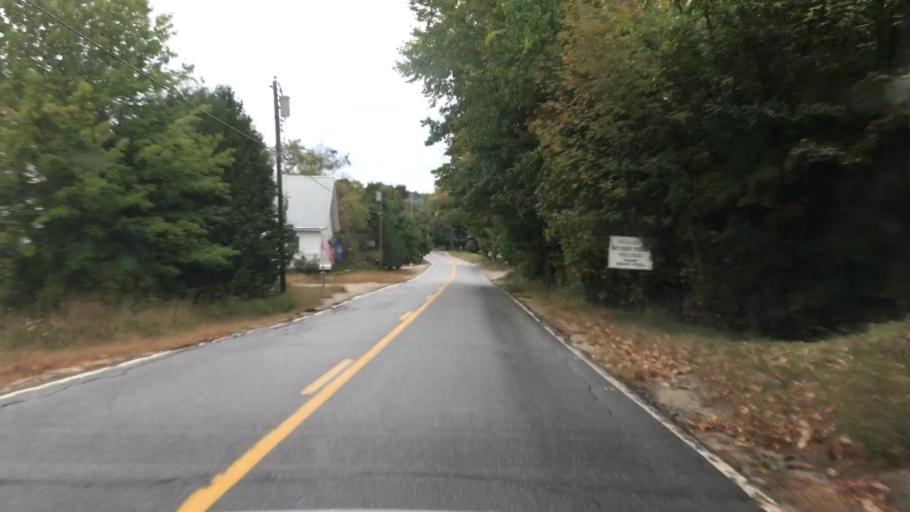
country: US
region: Maine
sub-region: Cumberland County
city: Raymond
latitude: 43.9820
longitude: -70.4733
